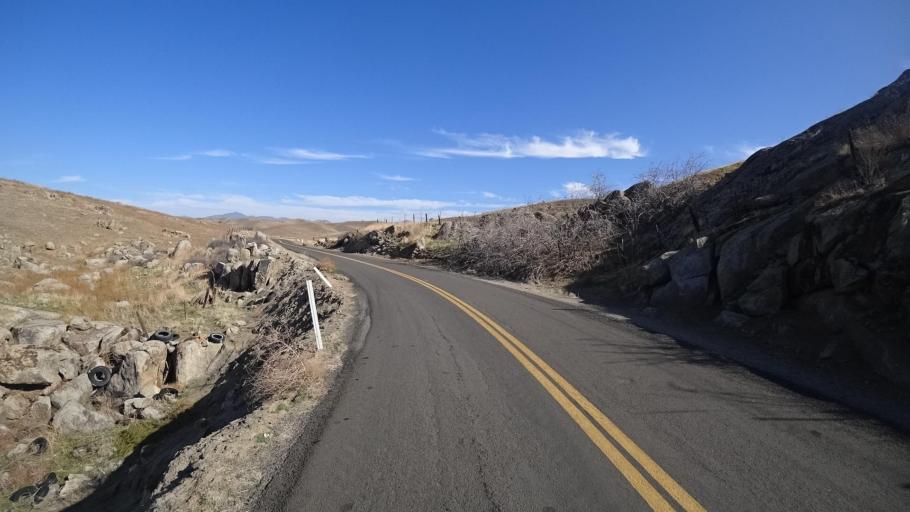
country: US
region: California
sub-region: Tulare County
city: Richgrove
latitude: 35.6733
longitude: -118.9000
